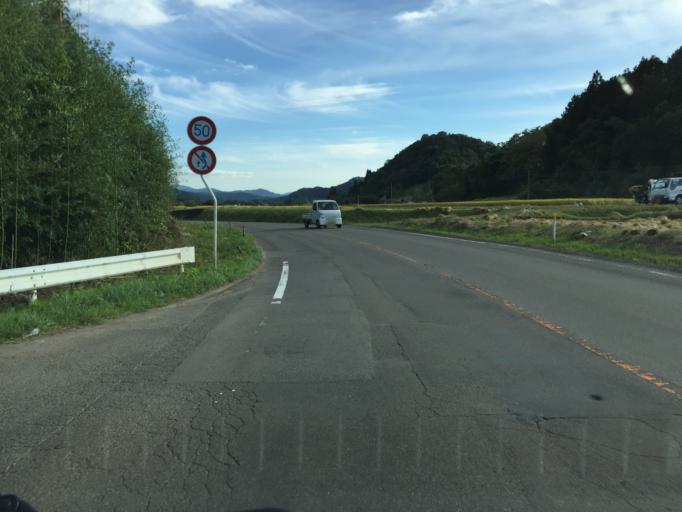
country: JP
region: Fukushima
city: Yanagawamachi-saiwaicho
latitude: 37.8413
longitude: 140.6145
